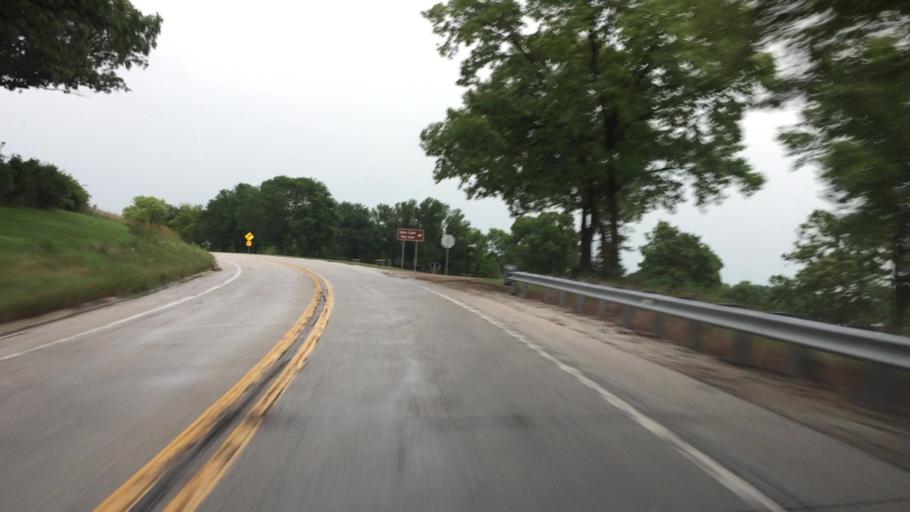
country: US
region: Illinois
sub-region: Hancock County
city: Nauvoo
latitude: 40.5202
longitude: -91.3640
